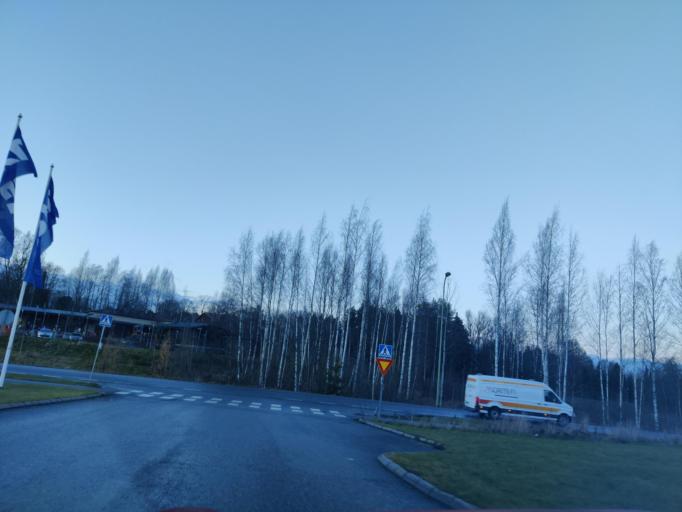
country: FI
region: Pirkanmaa
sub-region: Tampere
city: Nokia
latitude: 61.4682
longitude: 23.5111
